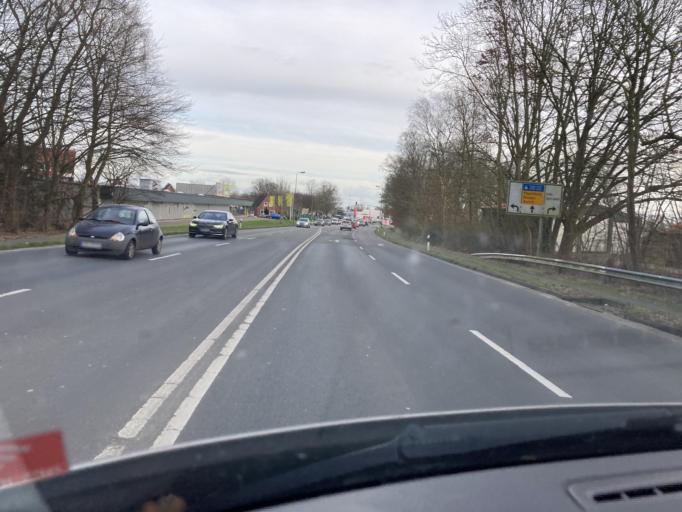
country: DE
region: Lower Saxony
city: Leer
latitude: 53.2223
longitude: 7.4707
